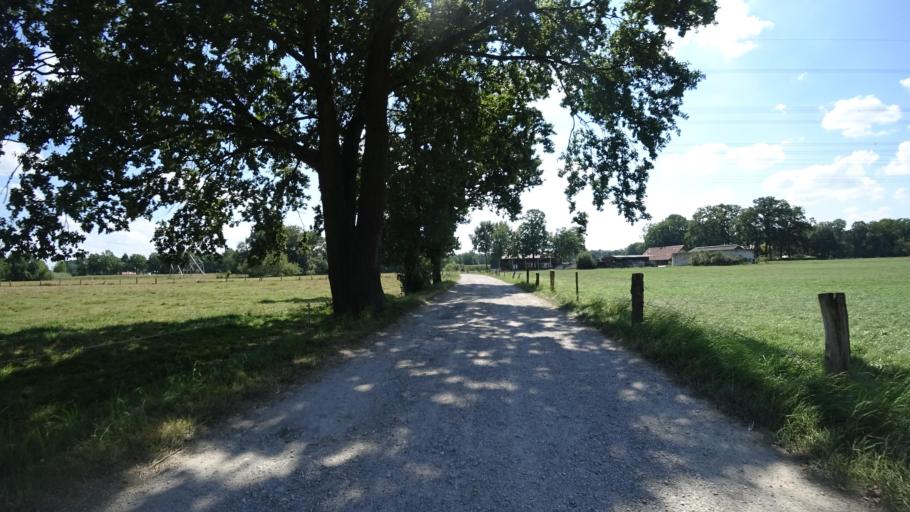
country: DE
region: North Rhine-Westphalia
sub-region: Regierungsbezirk Detmold
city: Guetersloh
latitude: 51.9326
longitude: 8.3978
